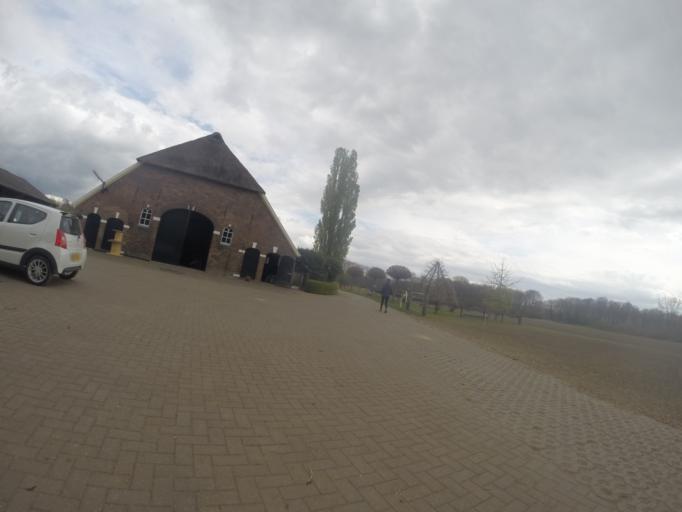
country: NL
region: Gelderland
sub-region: Gemeente Bronckhorst
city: Baak
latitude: 52.0957
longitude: 6.2723
